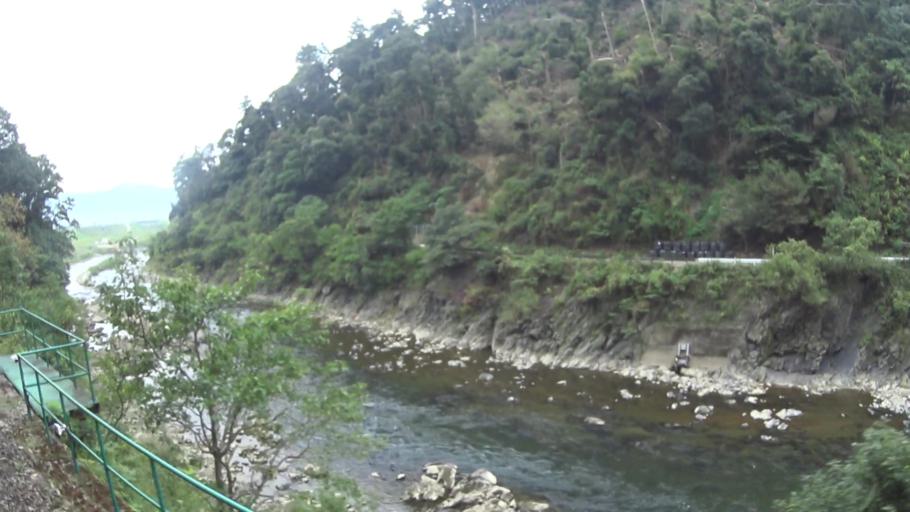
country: JP
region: Kyoto
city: Kameoka
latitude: 35.0165
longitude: 135.6101
